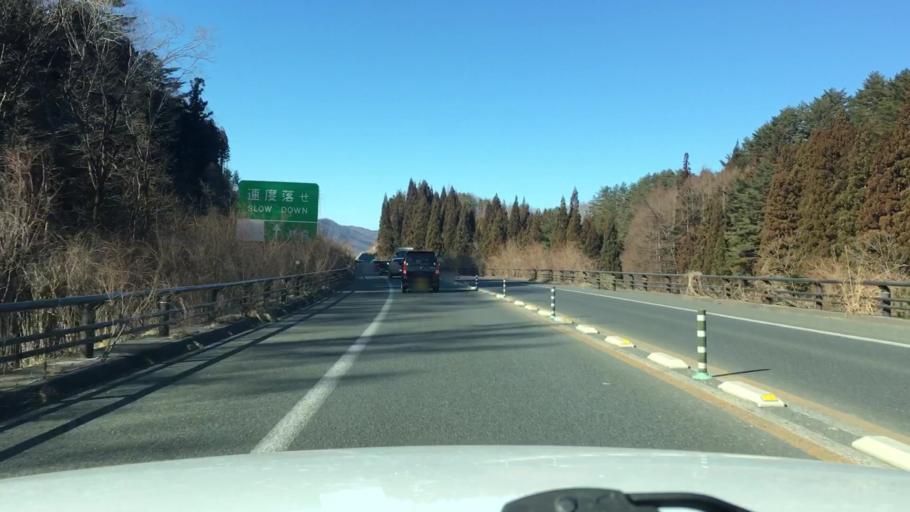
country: JP
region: Iwate
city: Miyako
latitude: 39.6162
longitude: 141.9339
